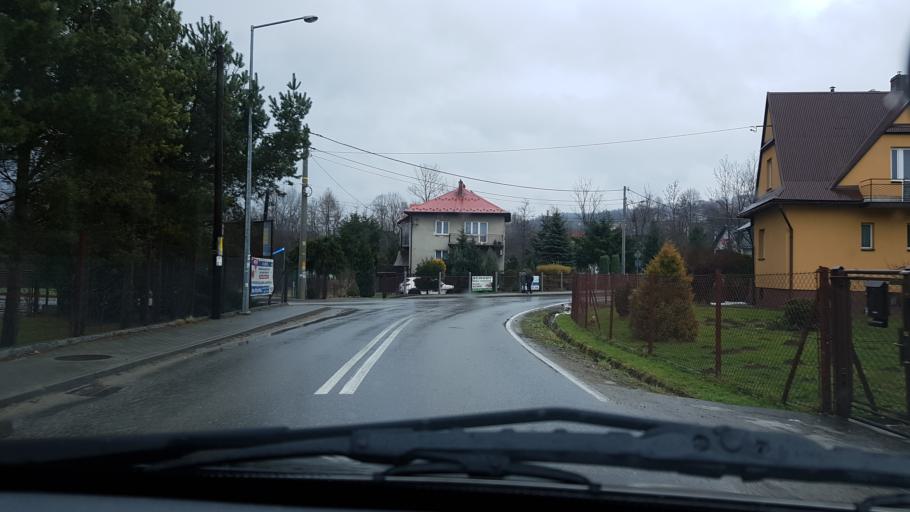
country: PL
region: Lesser Poland Voivodeship
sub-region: Powiat nowotarski
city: Raba Wyzna
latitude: 49.5672
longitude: 19.8786
